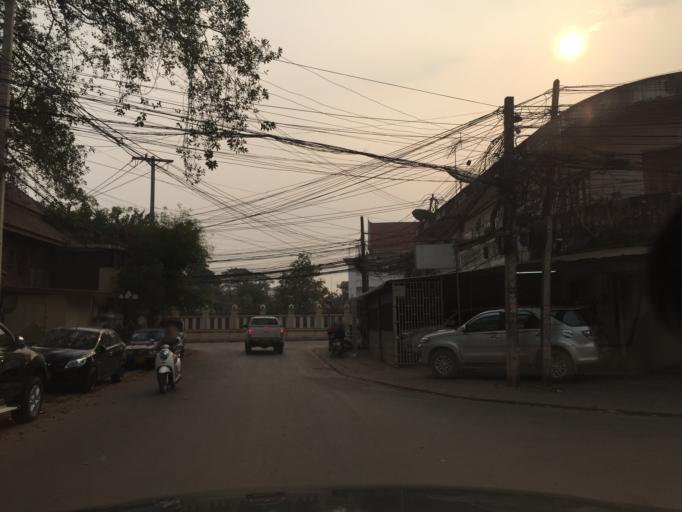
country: LA
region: Vientiane
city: Vientiane
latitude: 17.9743
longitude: 102.6159
